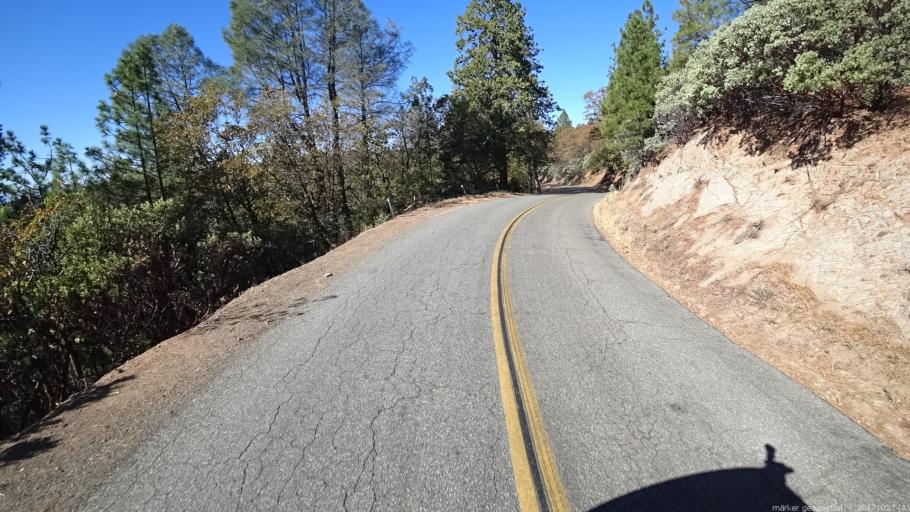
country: US
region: California
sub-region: Shasta County
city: Bella Vista
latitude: 40.7211
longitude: -122.0189
